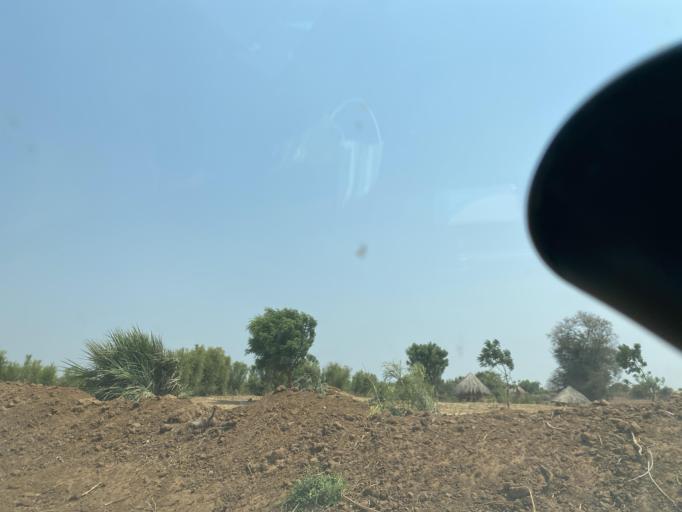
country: ZW
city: Chirundu
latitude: -16.1513
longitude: 28.8009
